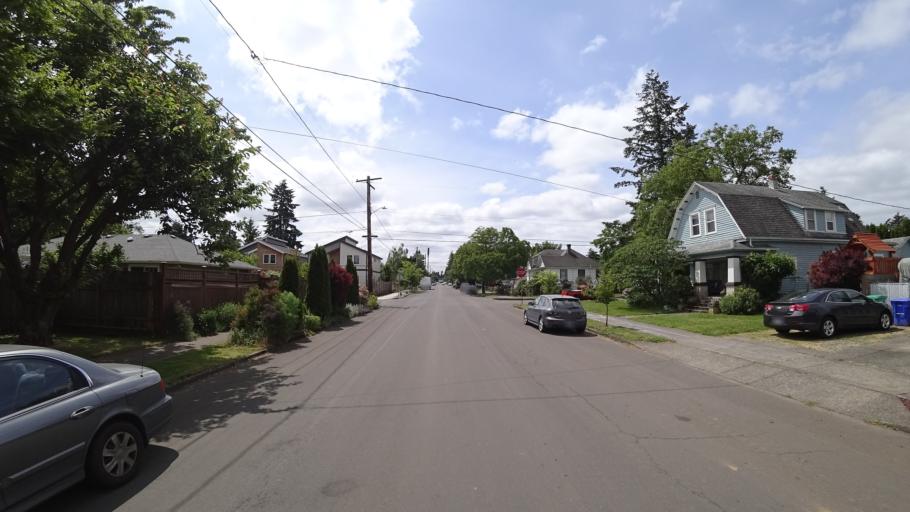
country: US
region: Oregon
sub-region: Multnomah County
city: Lents
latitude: 45.4813
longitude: -122.5944
